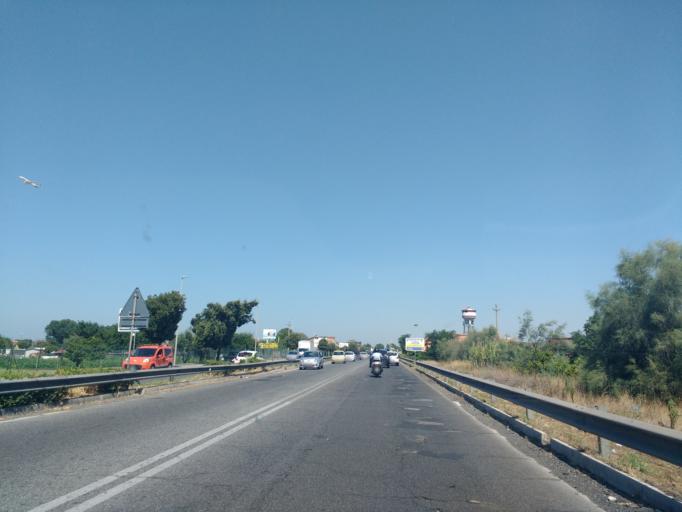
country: IT
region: Latium
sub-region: Citta metropolitana di Roma Capitale
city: Lido di Ostia
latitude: 41.7634
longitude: 12.2660
